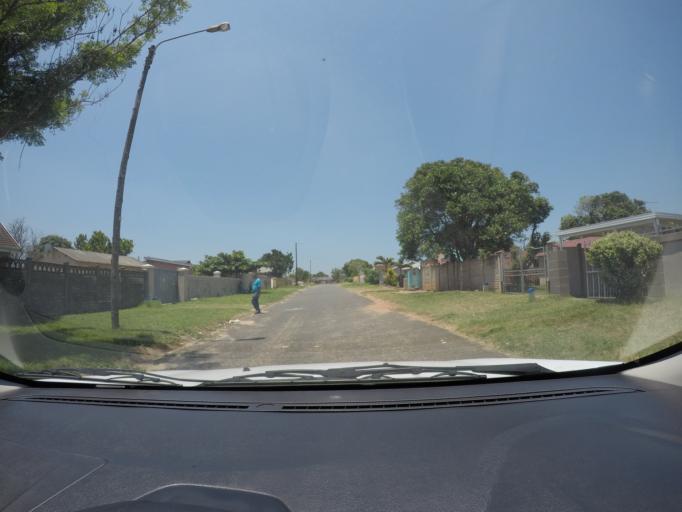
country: ZA
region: KwaZulu-Natal
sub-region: uThungulu District Municipality
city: eSikhawini
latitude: -28.8763
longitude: 31.9056
